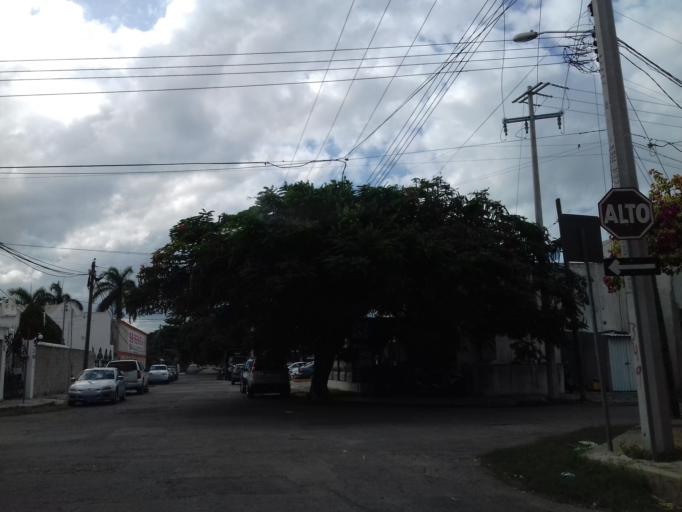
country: MX
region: Yucatan
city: Merida
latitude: 21.0012
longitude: -89.6144
